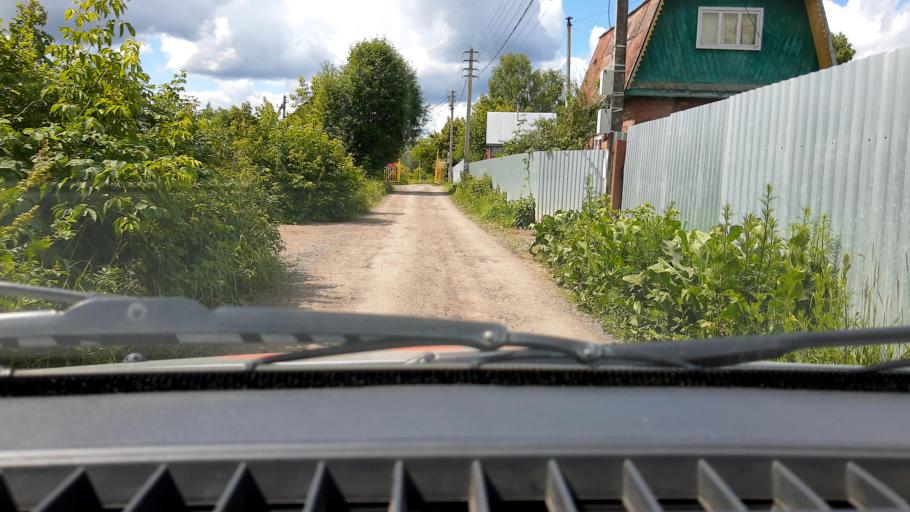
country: RU
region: Bashkortostan
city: Ufa
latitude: 54.6935
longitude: 56.0514
